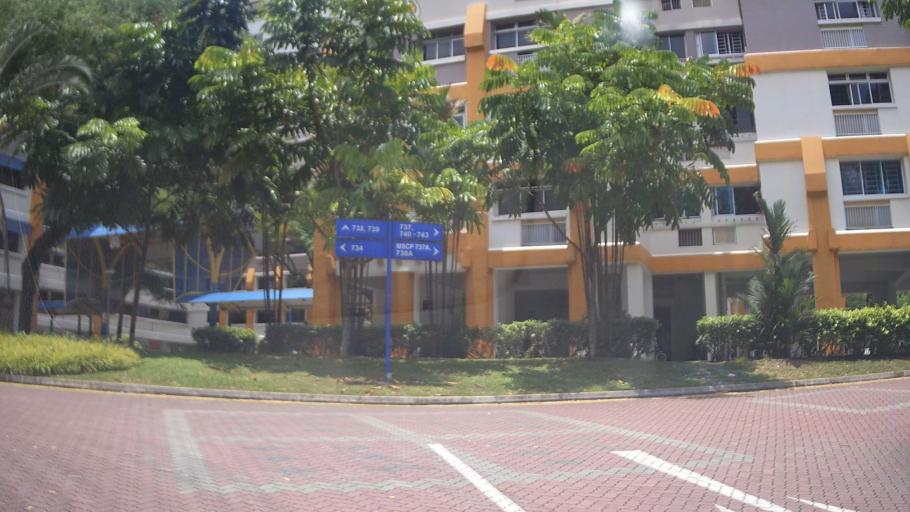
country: MY
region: Johor
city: Johor Bahru
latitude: 1.4445
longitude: 103.7968
